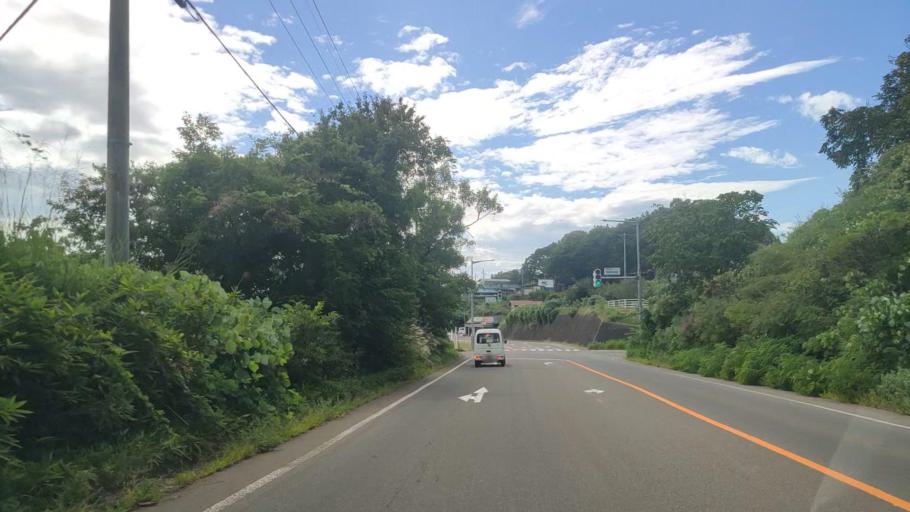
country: JP
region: Nagano
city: Nakano
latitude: 36.7572
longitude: 138.3174
